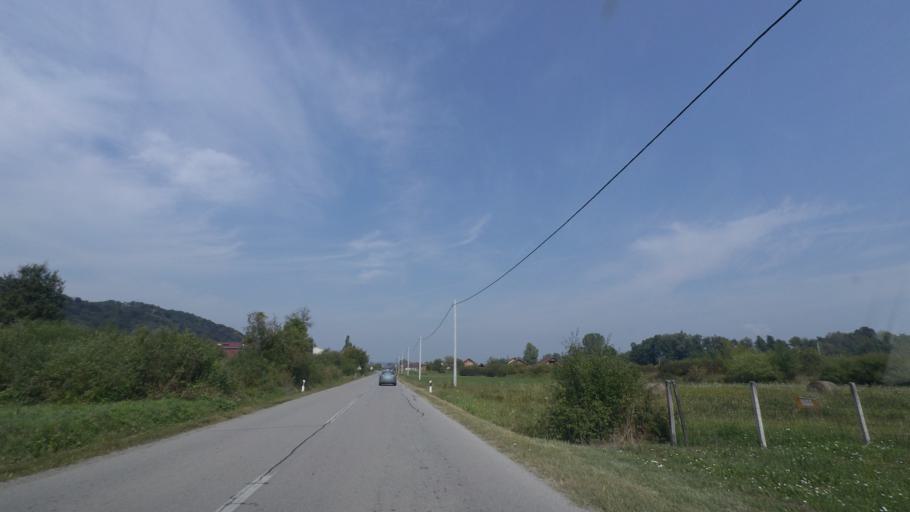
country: HR
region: Sisacko-Moslavacka
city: Glina
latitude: 45.3176
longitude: 16.1112
